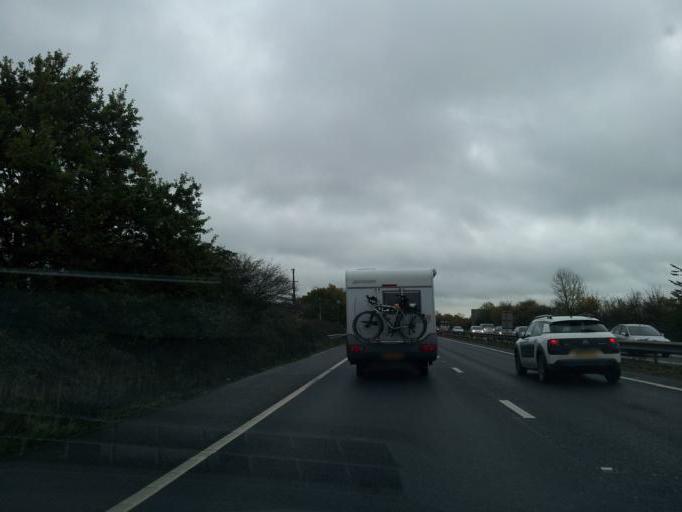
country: GB
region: England
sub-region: Oxfordshire
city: Bicester
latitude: 51.8600
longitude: -1.2127
